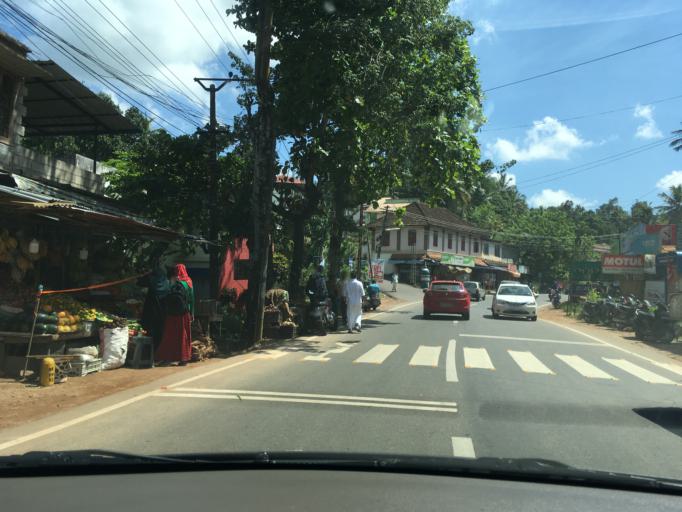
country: IN
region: Kerala
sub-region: Thiruvananthapuram
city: Nedumangad
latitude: 8.5750
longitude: 76.9967
